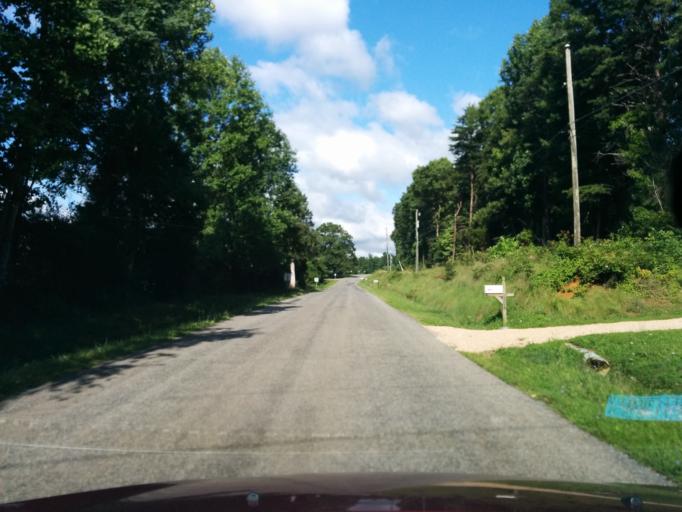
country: US
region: Virginia
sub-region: Rockbridge County
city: Glasgow
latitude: 37.6511
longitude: -79.5162
